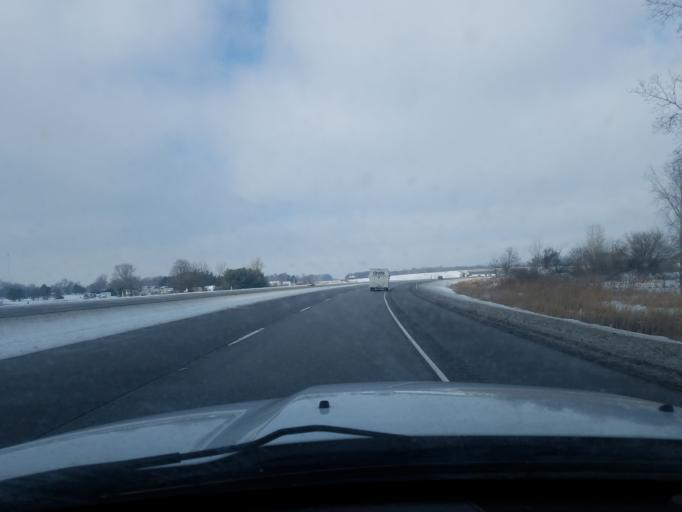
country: US
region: Indiana
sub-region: Marshall County
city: Plymouth
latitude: 41.4104
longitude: -86.2966
